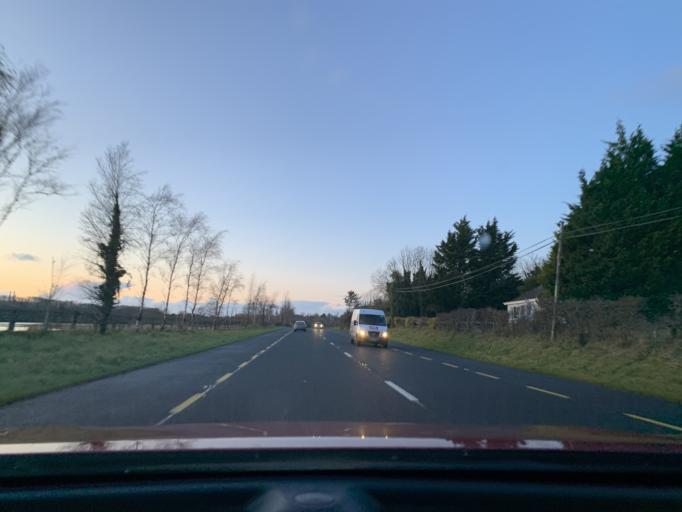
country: IE
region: Connaught
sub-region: County Leitrim
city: Carrick-on-Shannon
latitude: 53.9144
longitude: -7.9719
